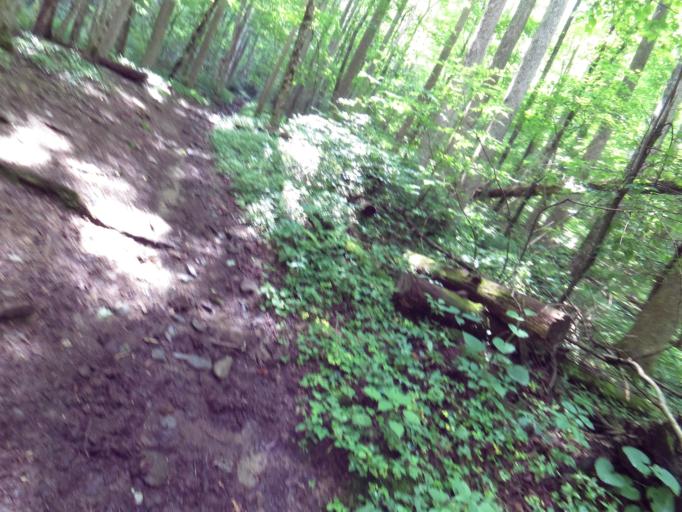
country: US
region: Tennessee
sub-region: Blount County
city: Wildwood
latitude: 35.5867
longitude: -83.7518
